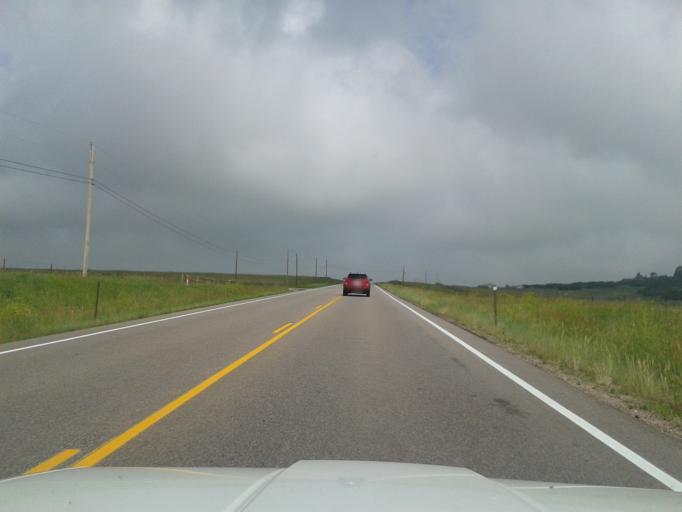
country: US
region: Colorado
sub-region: Elbert County
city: Elizabeth
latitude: 39.2669
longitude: -104.7260
